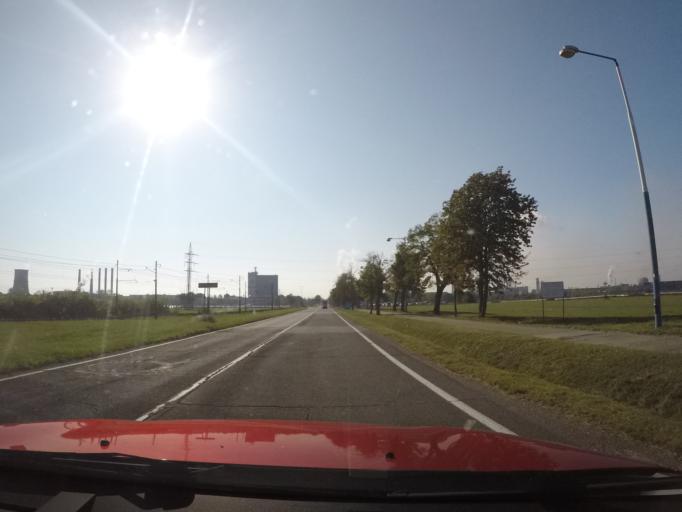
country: SK
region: Kosicky
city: Kosice
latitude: 48.6270
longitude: 21.1857
